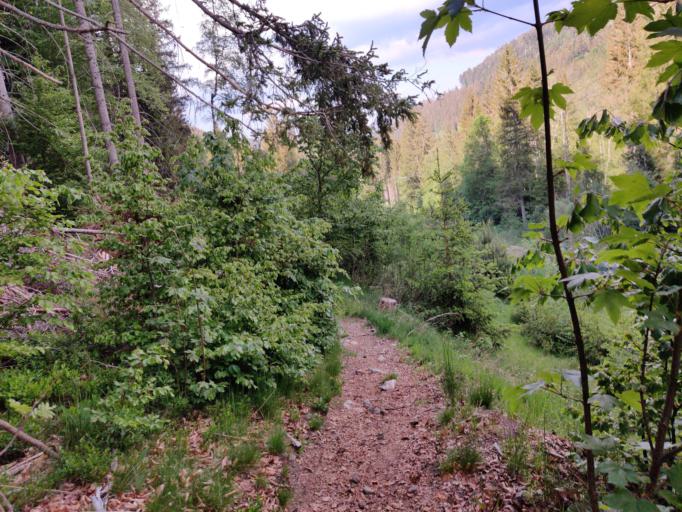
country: DE
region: Baden-Wuerttemberg
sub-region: Freiburg Region
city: Hinterzarten
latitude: 47.8763
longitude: 8.1042
